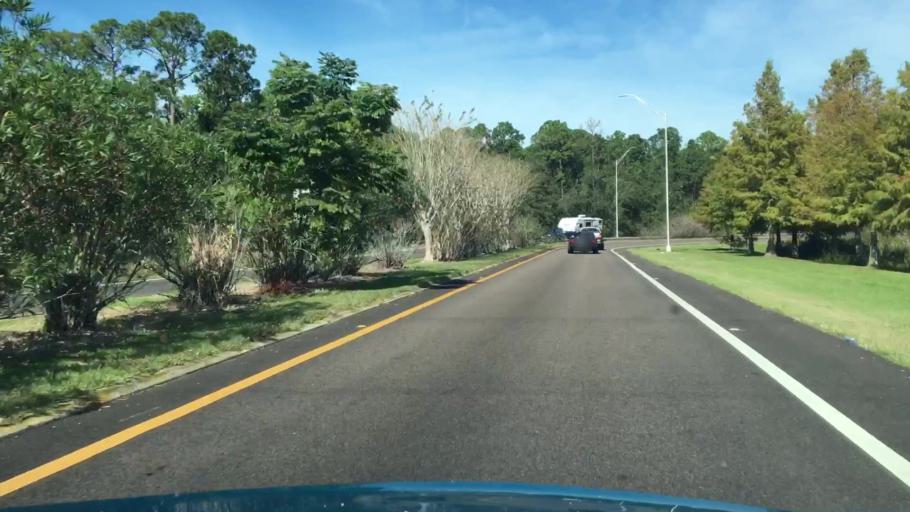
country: US
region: Florida
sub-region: Volusia County
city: DeBary
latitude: 28.8730
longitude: -81.2856
